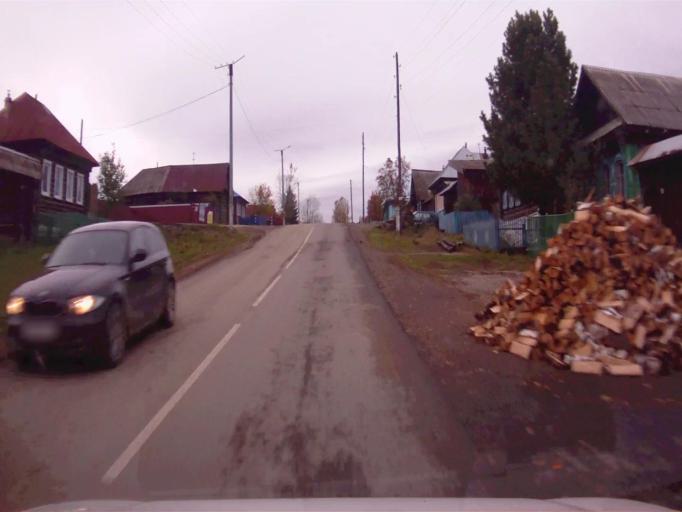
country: RU
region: Chelyabinsk
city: Nyazepetrovsk
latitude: 56.0602
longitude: 59.5801
